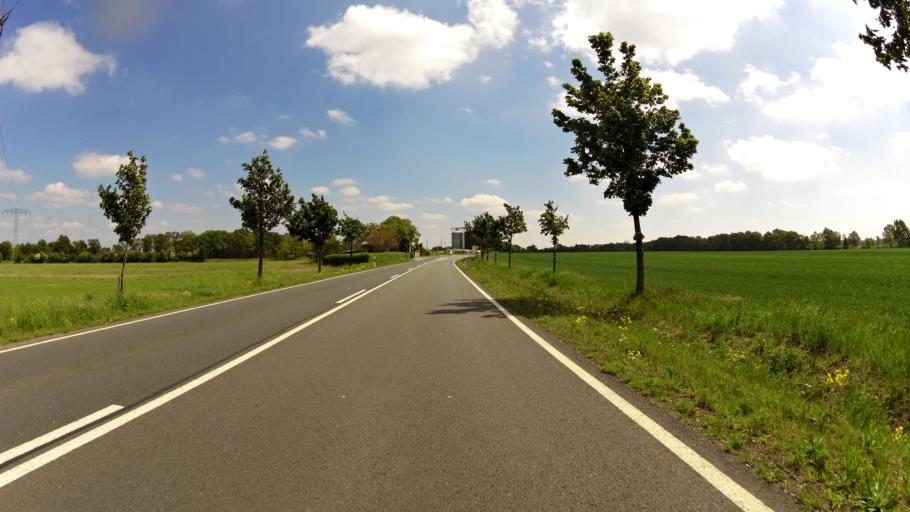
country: DE
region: Saxony
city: Belgern
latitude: 51.4892
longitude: 13.0963
